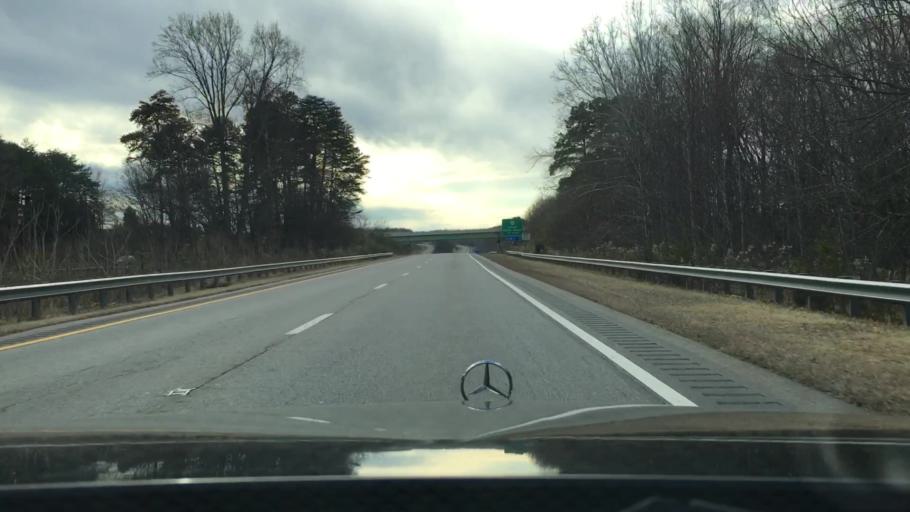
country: US
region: Virginia
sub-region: Pittsylvania County
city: Gretna
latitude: 36.9678
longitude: -79.3653
